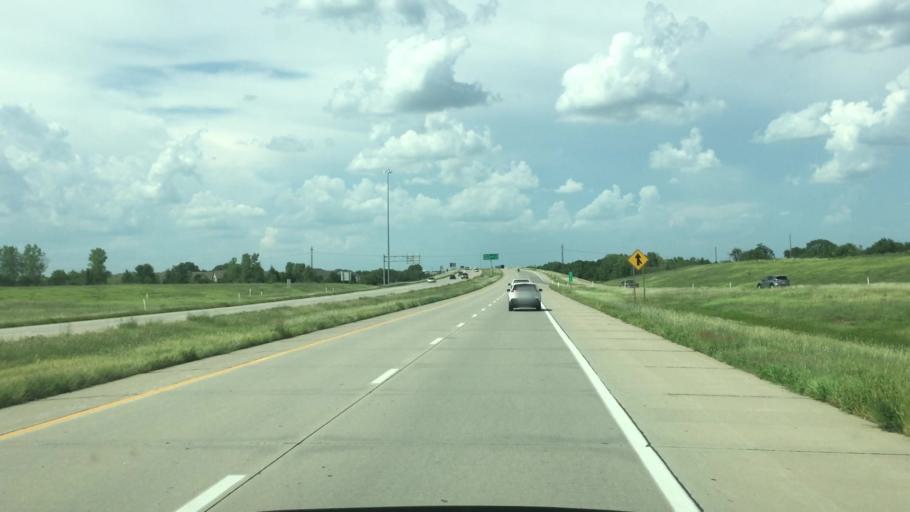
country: US
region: Kansas
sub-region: Butler County
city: Andover
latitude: 37.7099
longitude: -97.2001
